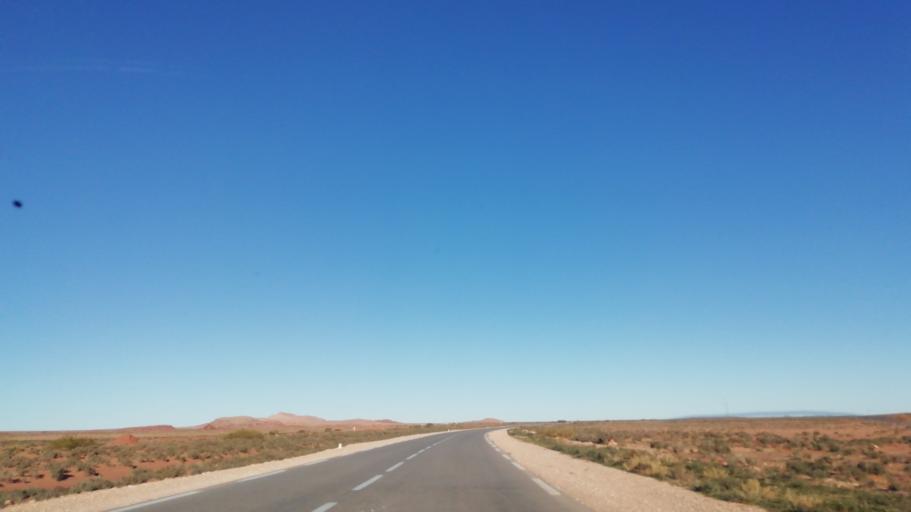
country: DZ
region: El Bayadh
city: El Abiodh Sidi Cheikh
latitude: 33.1095
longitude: 0.2217
